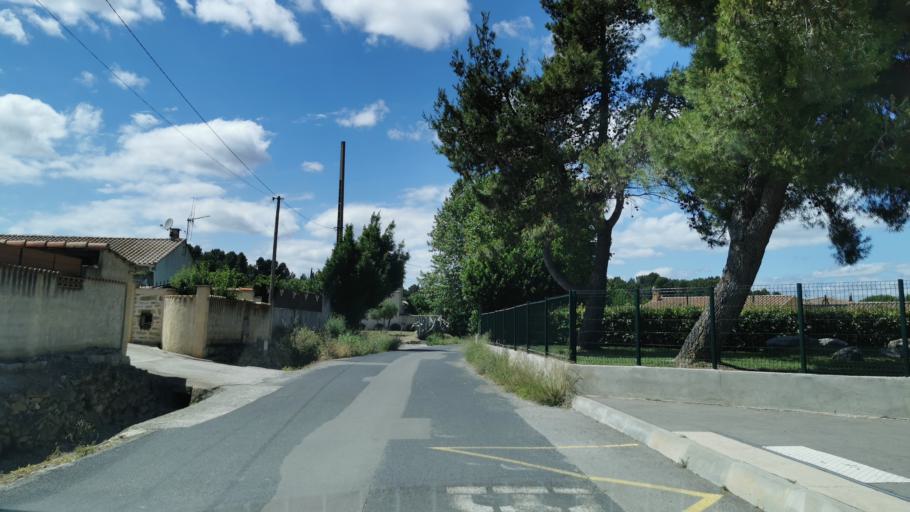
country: FR
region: Languedoc-Roussillon
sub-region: Departement de l'Aude
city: Moussan
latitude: 43.2323
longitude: 2.9473
